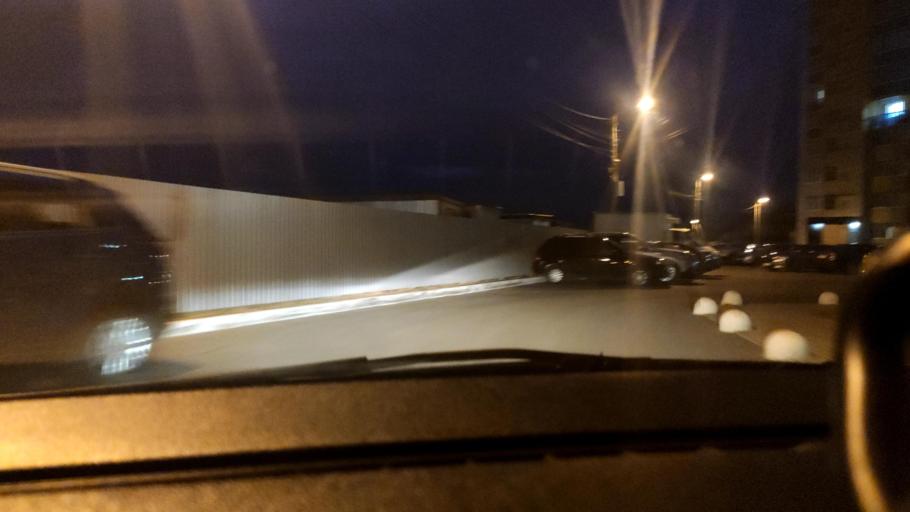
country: RU
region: Voronezj
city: Podgornoye
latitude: 51.7215
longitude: 39.1416
